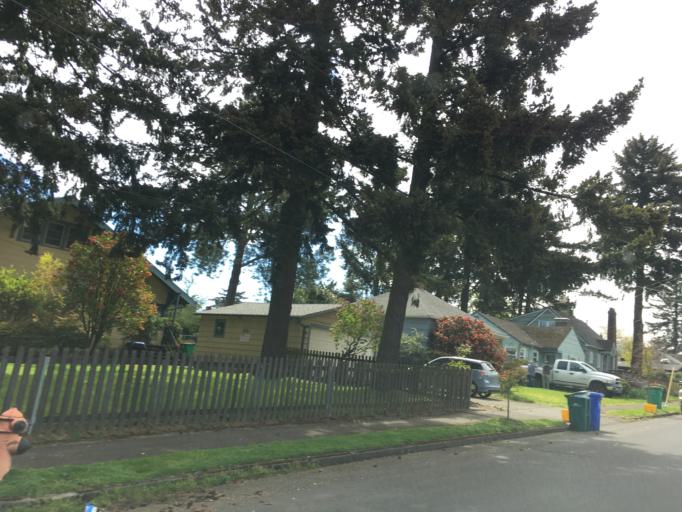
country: US
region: Oregon
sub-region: Multnomah County
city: Lents
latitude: 45.5336
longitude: -122.5858
